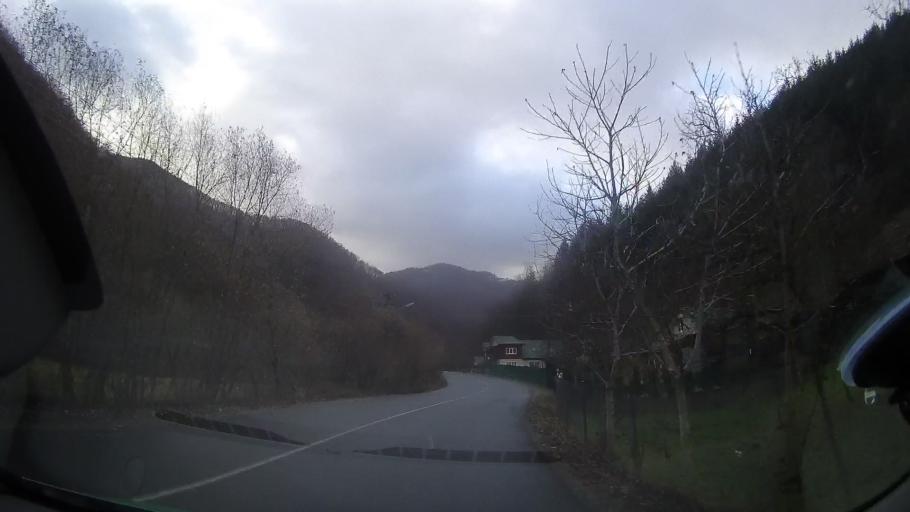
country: RO
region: Cluj
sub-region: Comuna Maguri-Racatau
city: Maguri-Racatau
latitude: 46.6722
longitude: 23.2529
